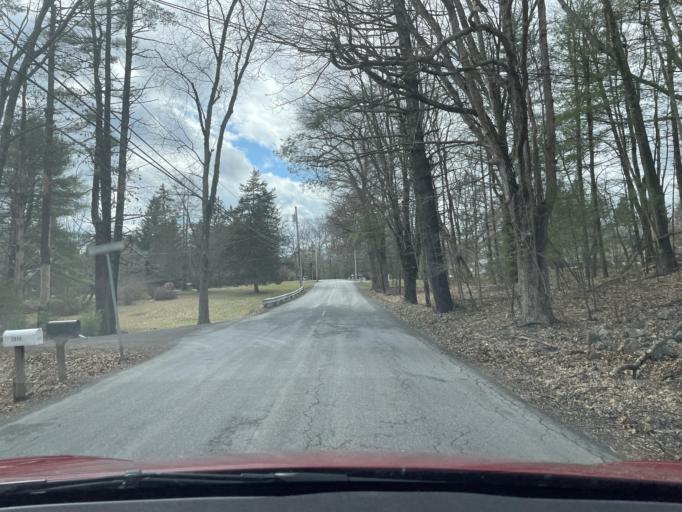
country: US
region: New York
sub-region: Ulster County
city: Zena
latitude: 42.0413
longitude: -74.0326
